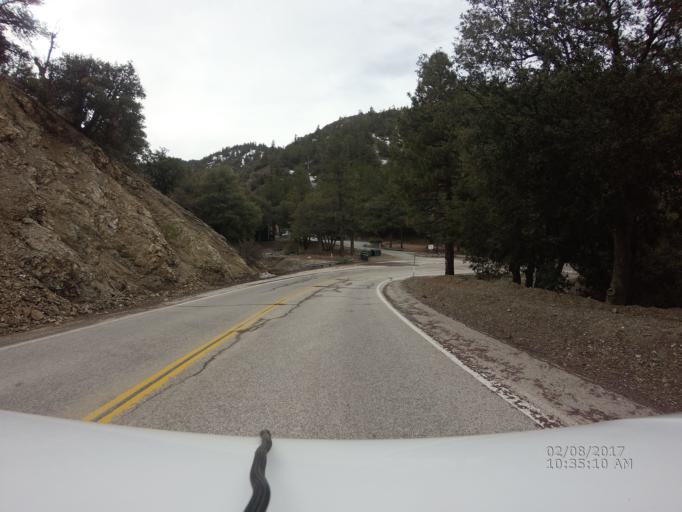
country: US
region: California
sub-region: San Bernardino County
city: Pinon Hills
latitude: 34.3988
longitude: -117.7472
